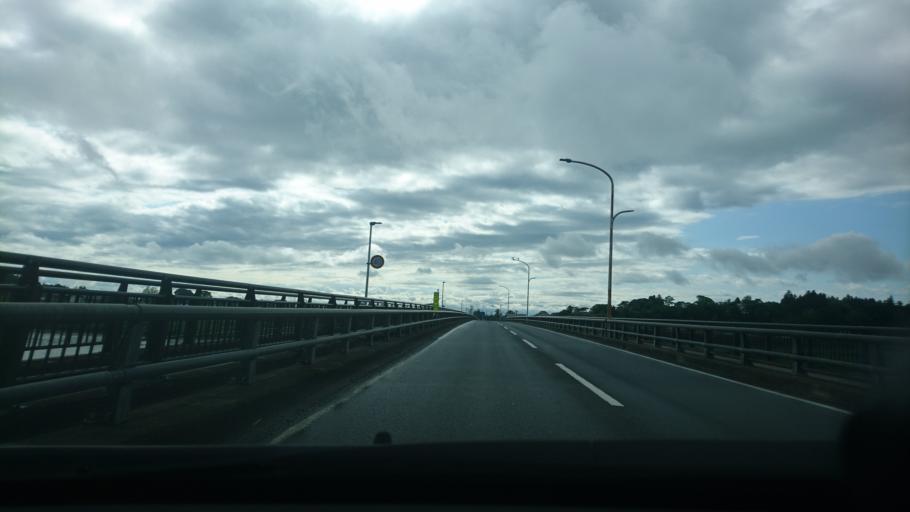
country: JP
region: Miyagi
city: Wakuya
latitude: 38.6527
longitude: 141.2871
